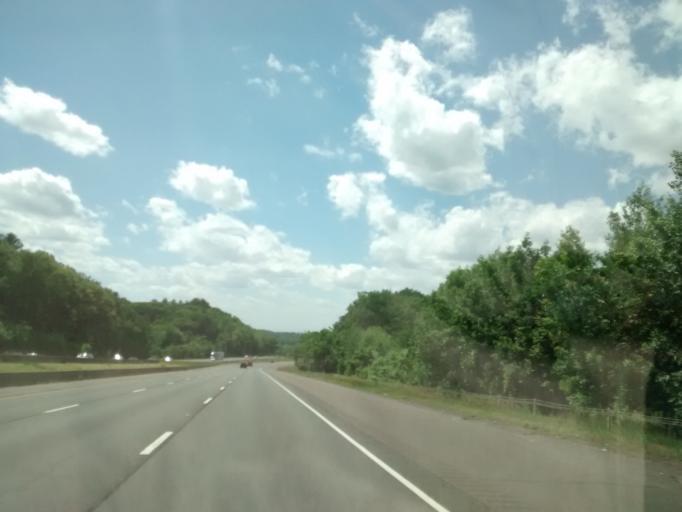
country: US
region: Connecticut
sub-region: Tolland County
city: Rockville
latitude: 41.8544
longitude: -72.4133
